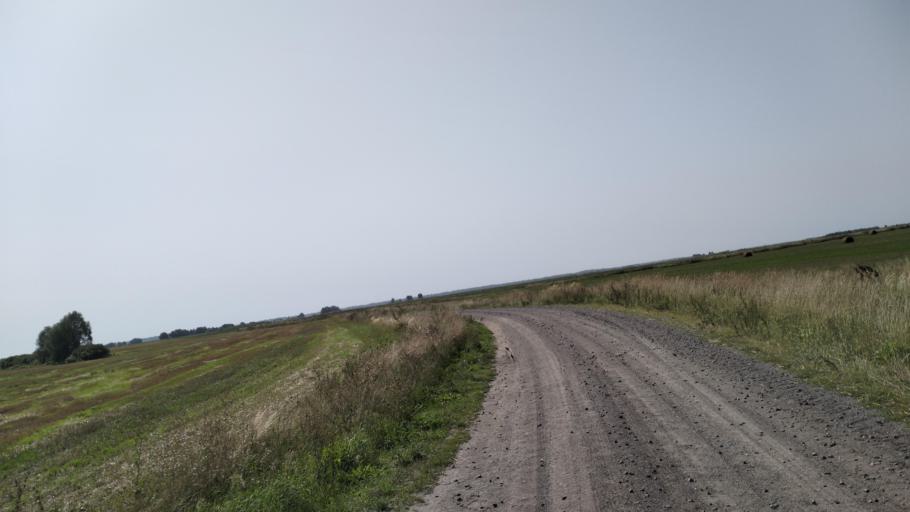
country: BY
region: Brest
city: Davyd-Haradok
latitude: 52.0109
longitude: 27.1659
